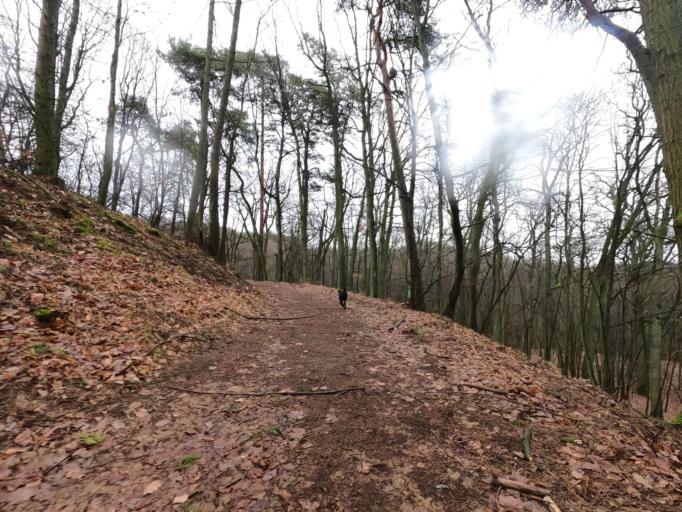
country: PL
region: Greater Poland Voivodeship
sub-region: Powiat pilski
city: Wyrzysk
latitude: 53.1266
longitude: 17.2638
